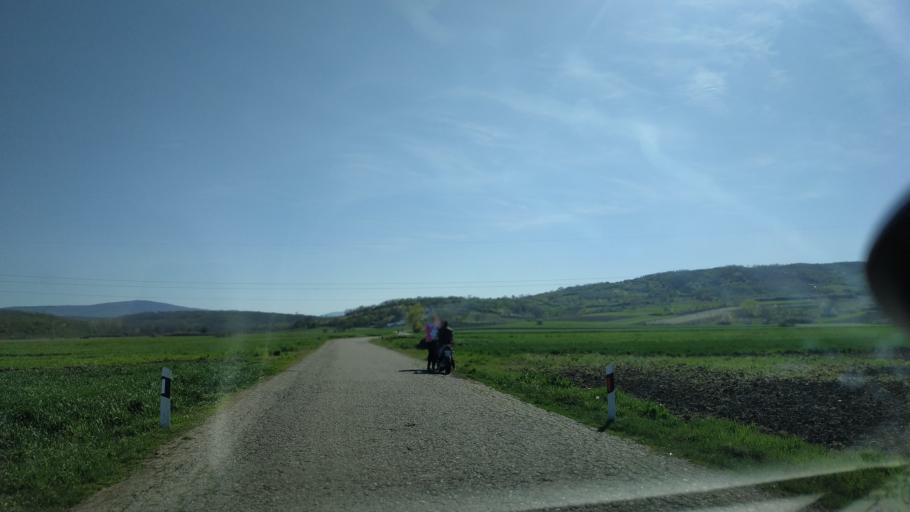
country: RS
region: Central Serbia
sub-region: Nisavski Okrug
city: Aleksinac
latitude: 43.5033
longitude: 21.6802
